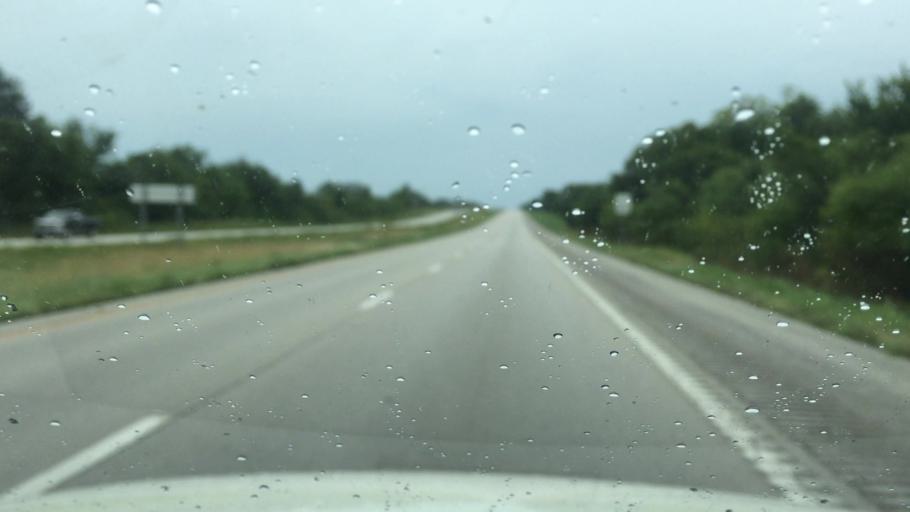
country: US
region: Missouri
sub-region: Jackson County
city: Lake Lotawana
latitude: 38.8827
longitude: -94.2225
